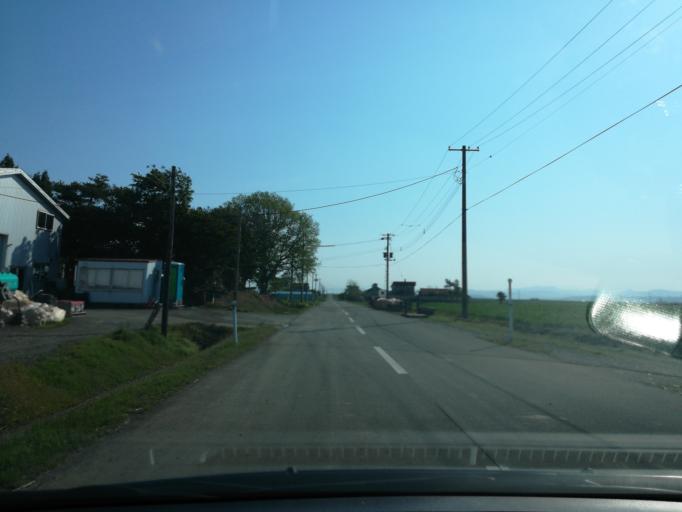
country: JP
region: Hokkaido
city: Iwamizawa
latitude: 43.1284
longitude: 141.6713
